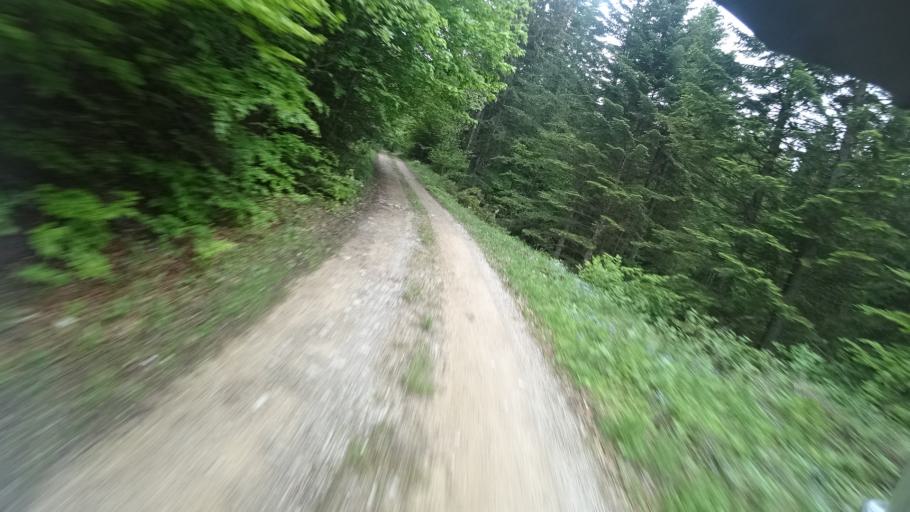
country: BA
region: Federation of Bosnia and Herzegovina
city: Bihac
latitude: 44.6351
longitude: 15.8188
